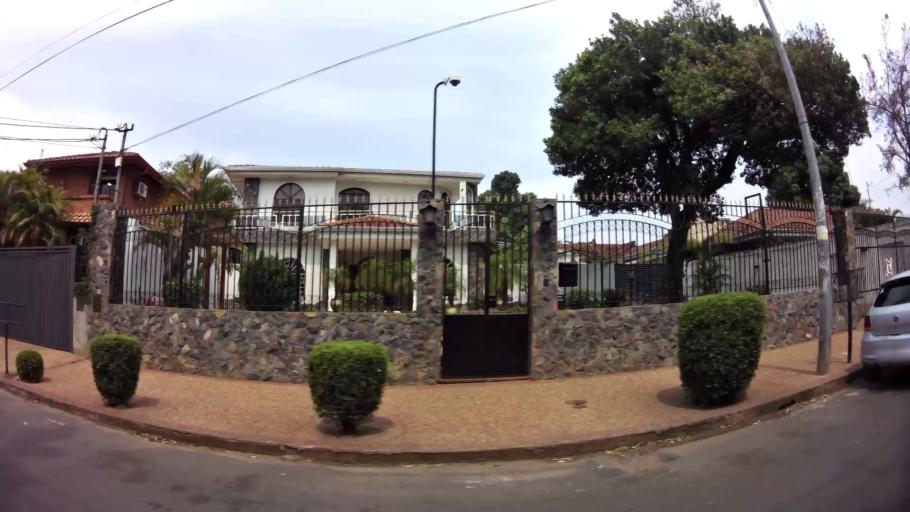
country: PY
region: Asuncion
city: Asuncion
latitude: -25.2885
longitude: -57.5820
